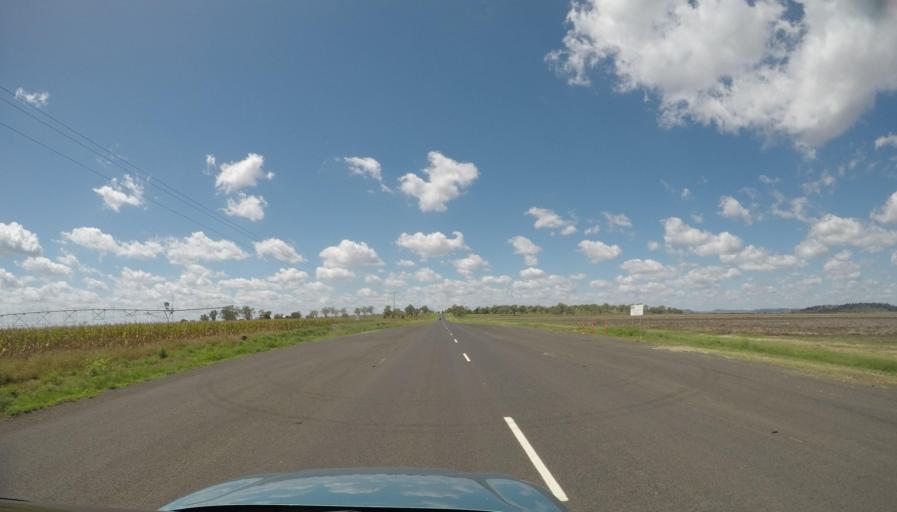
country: AU
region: Queensland
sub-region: Toowoomba
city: Oakey
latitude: -27.5275
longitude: 151.5803
